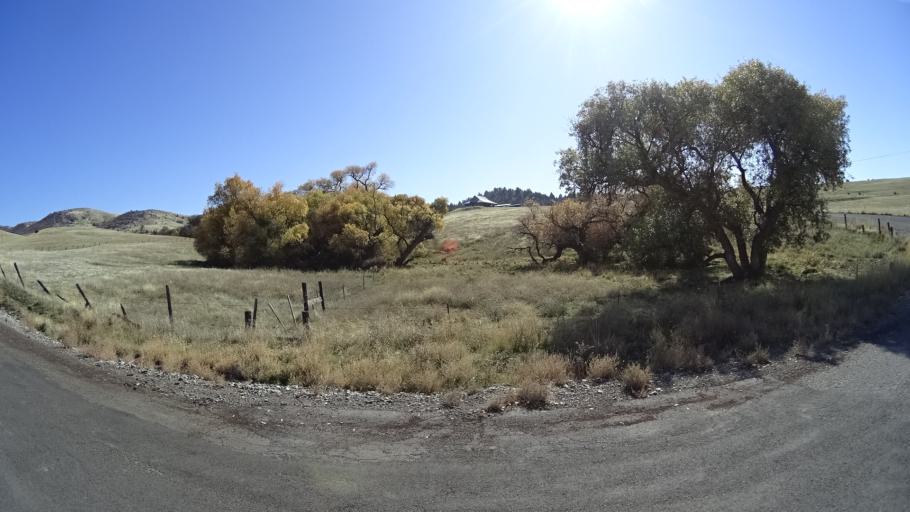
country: US
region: California
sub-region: Siskiyou County
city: Montague
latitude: 41.8138
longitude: -122.3766
